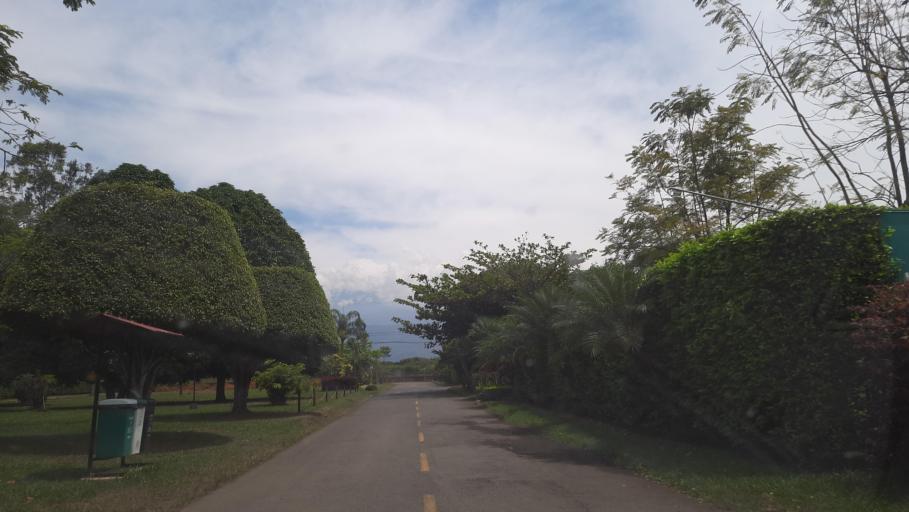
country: CO
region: Valle del Cauca
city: Jamundi
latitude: 3.2688
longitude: -76.5214
